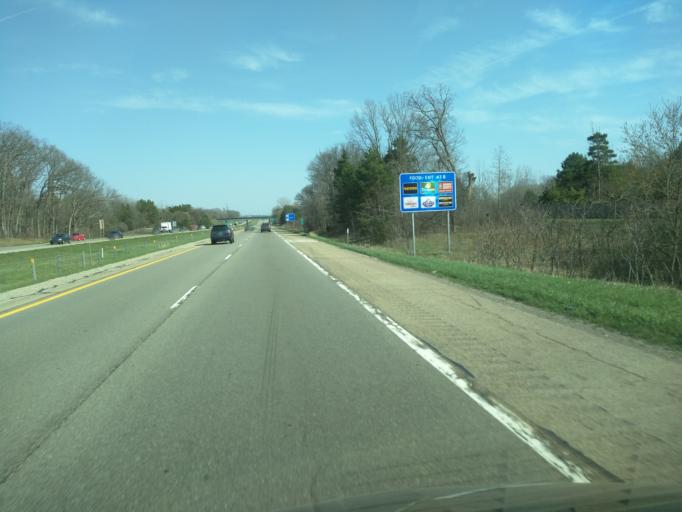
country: US
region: Michigan
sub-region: Kent County
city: East Grand Rapids
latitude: 42.9232
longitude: -85.5516
